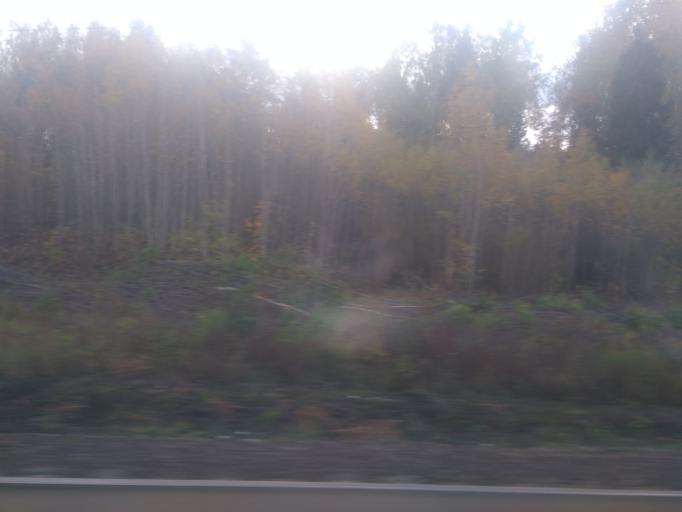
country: RU
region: Udmurtiya
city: Mozhga
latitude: 56.4265
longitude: 52.0452
